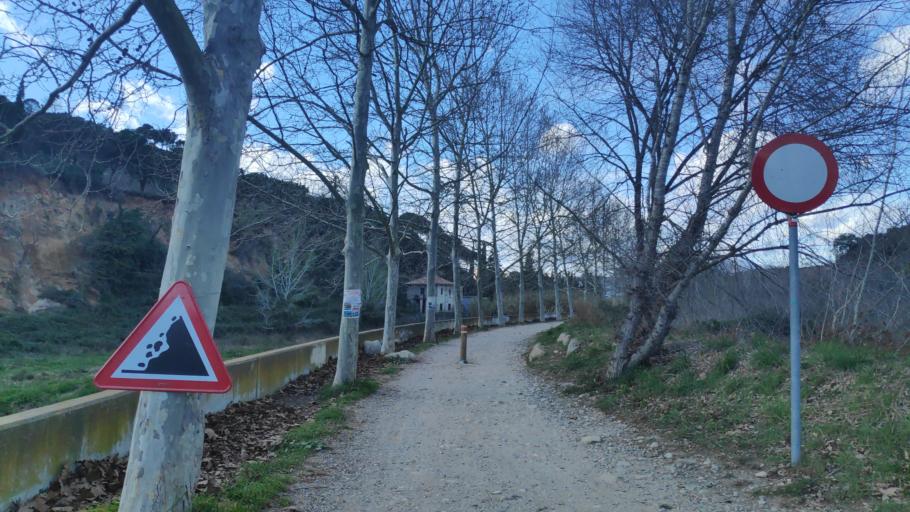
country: ES
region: Catalonia
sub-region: Provincia de Barcelona
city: Sabadell
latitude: 41.5574
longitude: 2.1156
